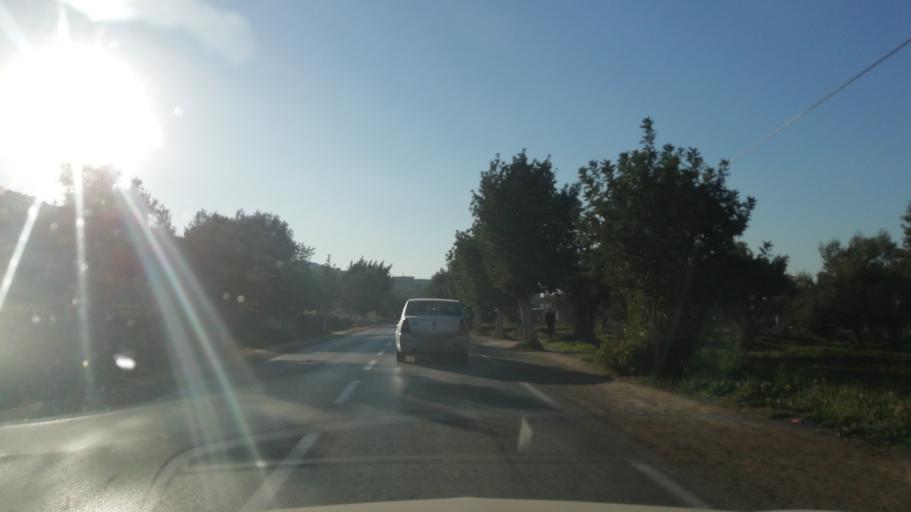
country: DZ
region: Tlemcen
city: Beni Mester
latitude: 34.8607
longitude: -1.4400
